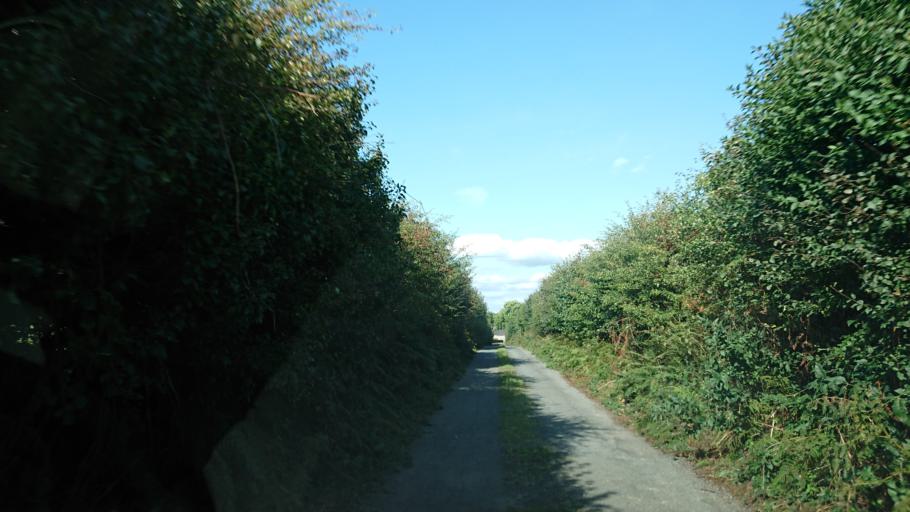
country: IE
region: Munster
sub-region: Waterford
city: Waterford
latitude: 52.2106
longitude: -7.0550
